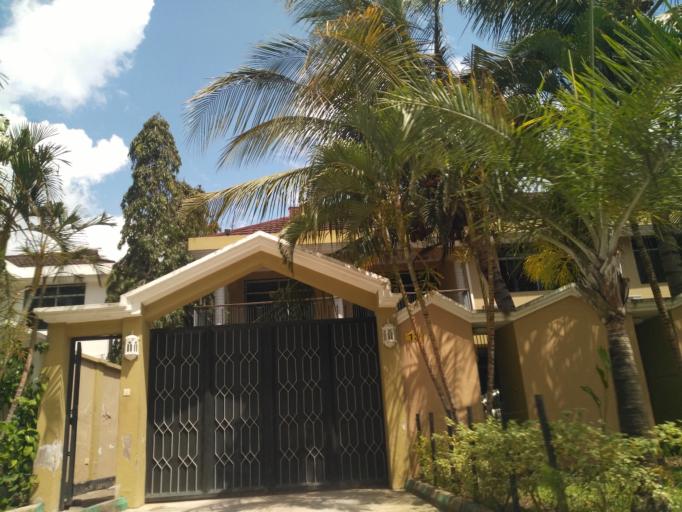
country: TZ
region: Dar es Salaam
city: Magomeni
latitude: -6.7617
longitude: 39.2492
